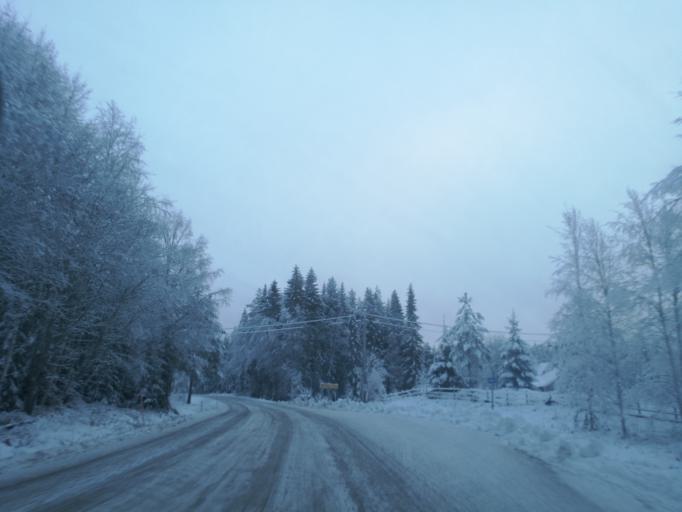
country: NO
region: Hedmark
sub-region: Grue
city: Kirkenaer
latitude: 60.4202
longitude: 12.4170
